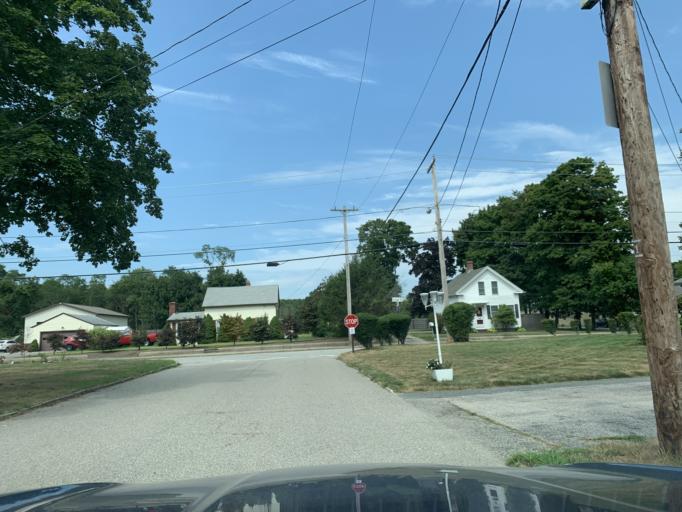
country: US
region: Rhode Island
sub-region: Kent County
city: East Greenwich
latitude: 41.6160
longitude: -71.4695
